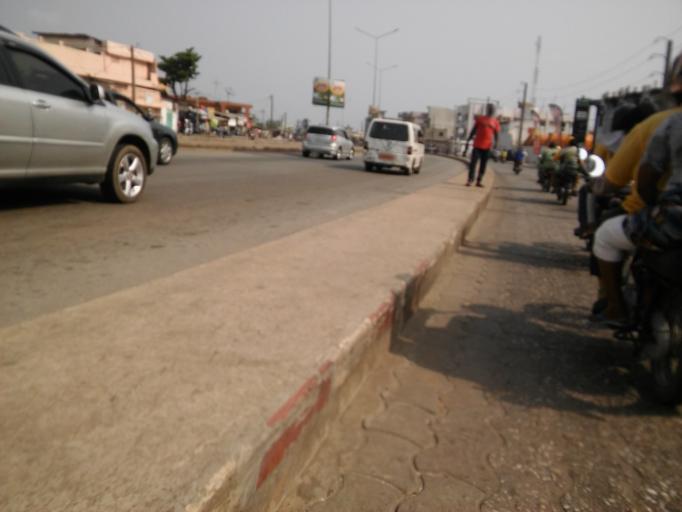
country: BJ
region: Littoral
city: Cotonou
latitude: 6.3809
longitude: 2.3793
